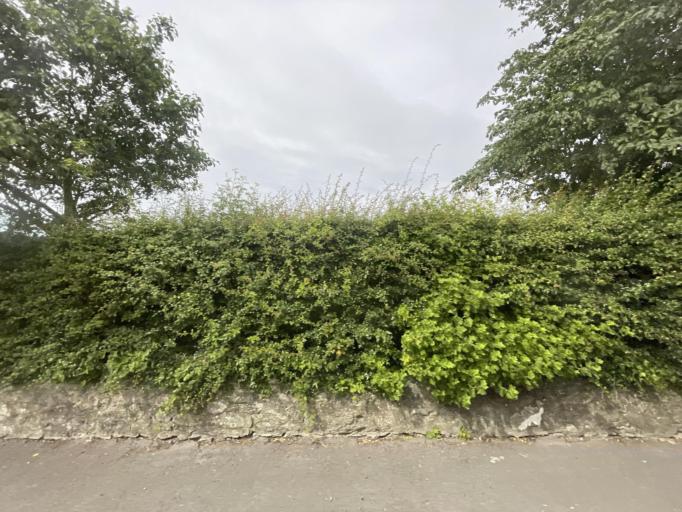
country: GB
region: Wales
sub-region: Anglesey
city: Menai Bridge
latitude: 53.2295
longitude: -4.1773
